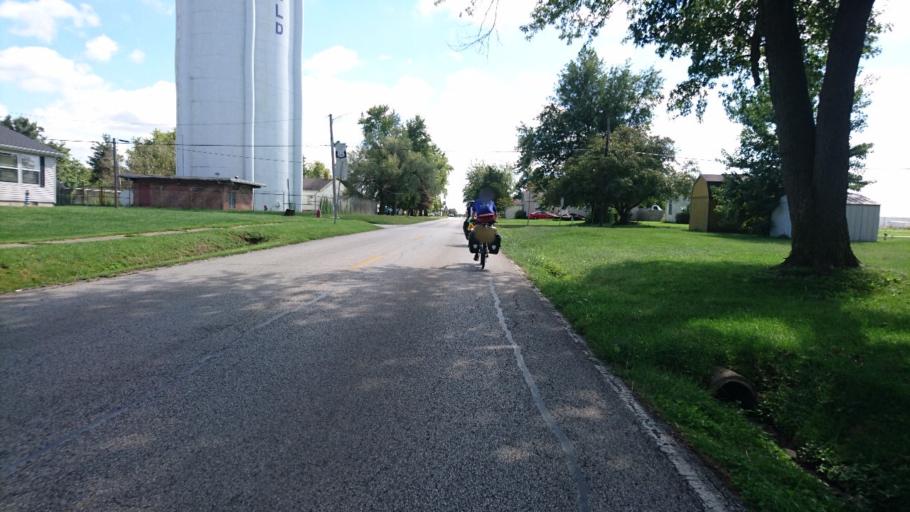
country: US
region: Illinois
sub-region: Montgomery County
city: Litchfield
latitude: 39.1725
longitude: -89.6668
